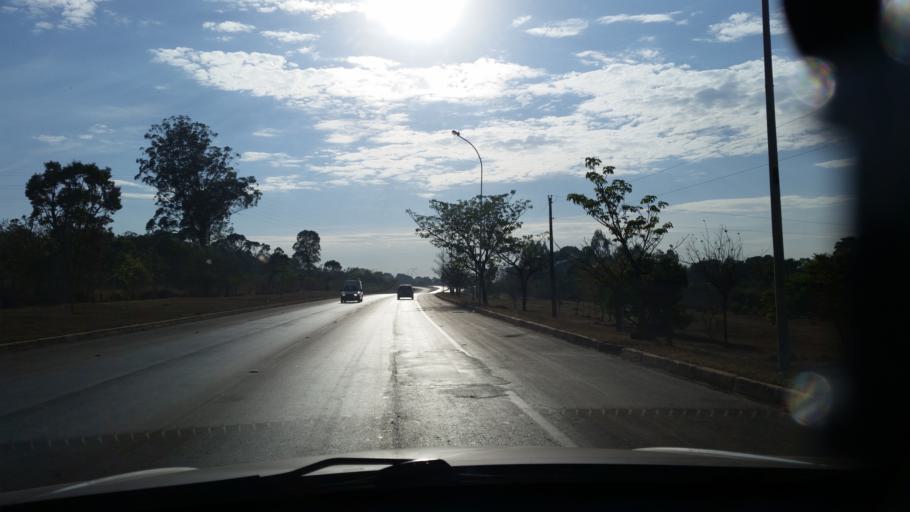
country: BR
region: Federal District
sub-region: Brasilia
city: Brasilia
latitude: -15.7245
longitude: -47.9023
